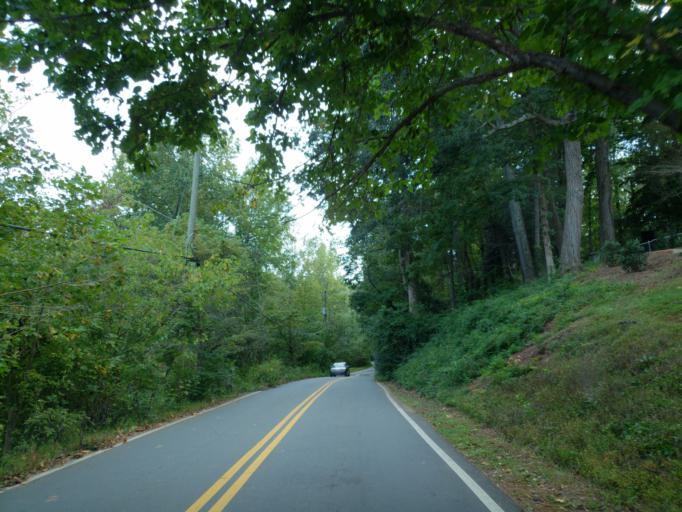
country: US
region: Georgia
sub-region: Fulton County
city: Roswell
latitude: 34.0842
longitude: -84.4160
